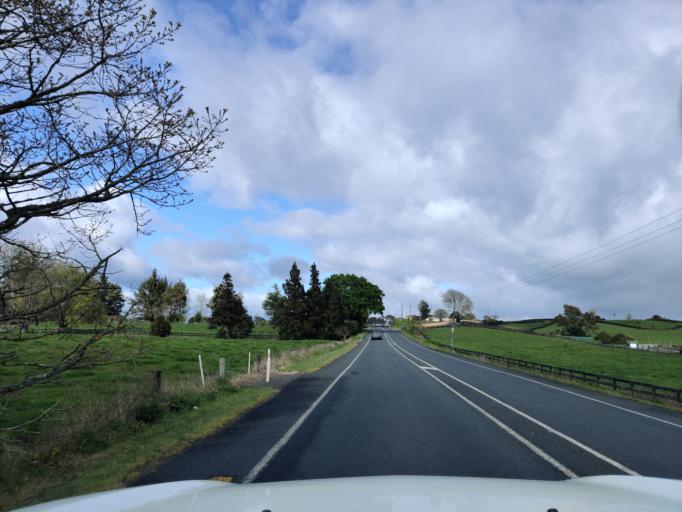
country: NZ
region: Waikato
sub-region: Hamilton City
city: Hamilton
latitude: -37.8130
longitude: 175.2332
